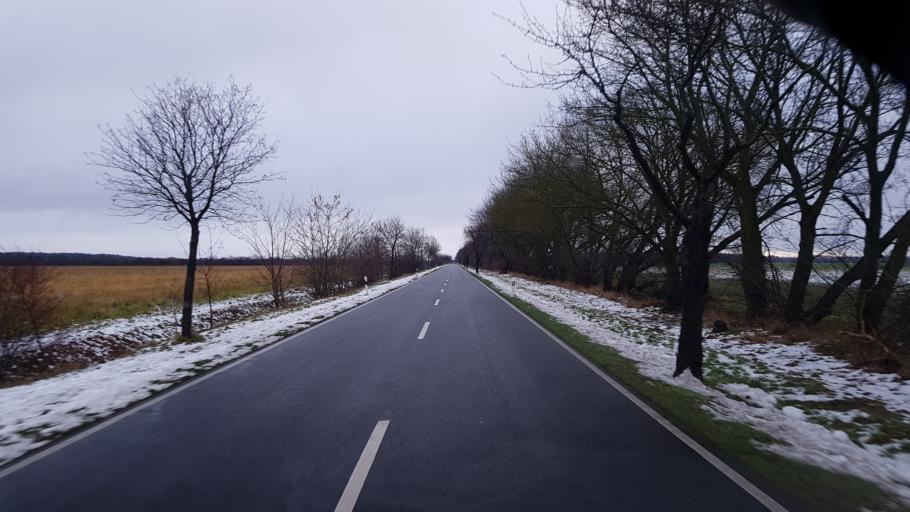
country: DE
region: Brandenburg
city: Luckau
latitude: 51.8501
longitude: 13.7650
